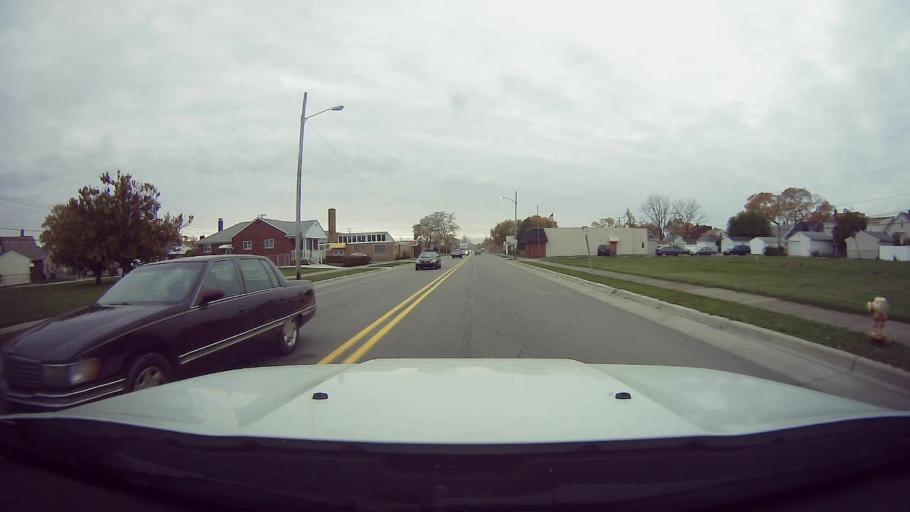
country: US
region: Michigan
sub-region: Wayne County
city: Dearborn
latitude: 42.3347
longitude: -83.1862
